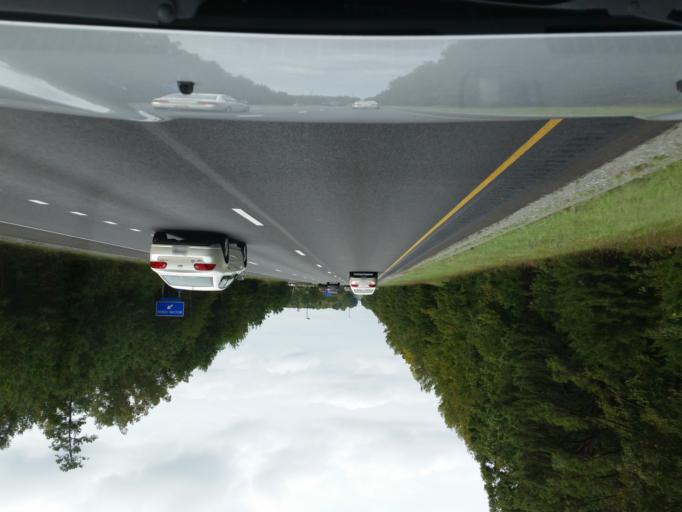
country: US
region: Virginia
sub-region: New Kent County
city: New Kent
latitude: 37.4983
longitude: -77.0486
